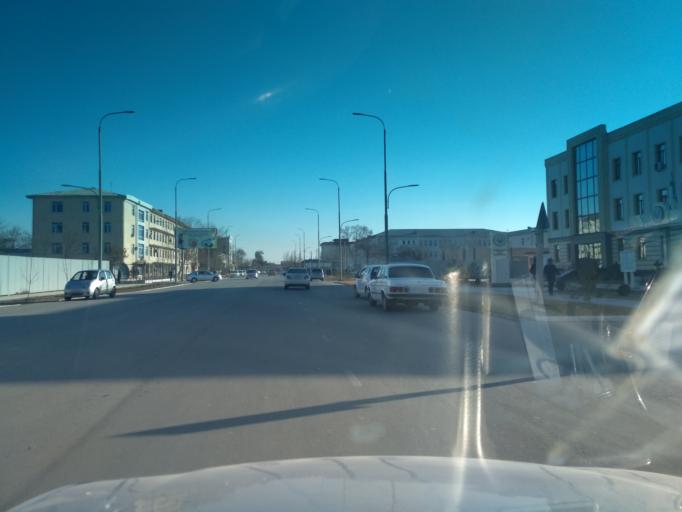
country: UZ
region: Sirdaryo
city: Guliston
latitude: 40.4978
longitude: 68.7705
